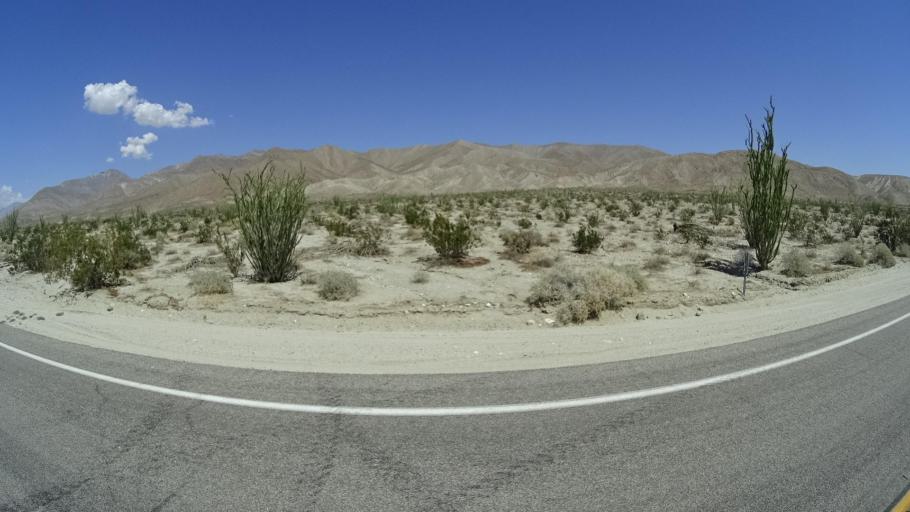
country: US
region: California
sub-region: Imperial County
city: Desert Shores
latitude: 33.2926
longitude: -116.1746
